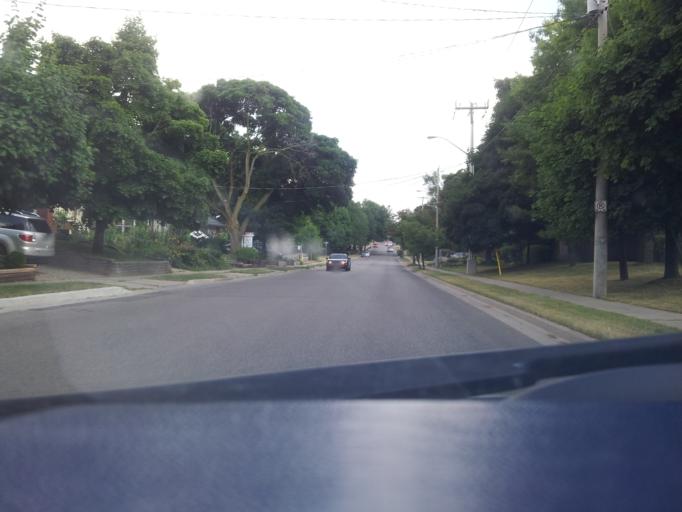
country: CA
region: Ontario
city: Kitchener
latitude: 43.4438
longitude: -80.5049
